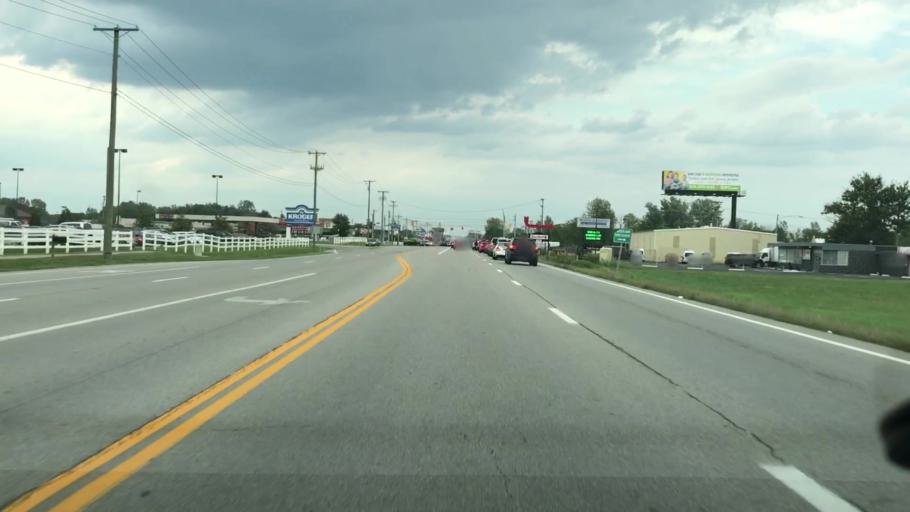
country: US
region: Ohio
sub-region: Franklin County
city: Lincoln Village
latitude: 39.9510
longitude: -83.1565
